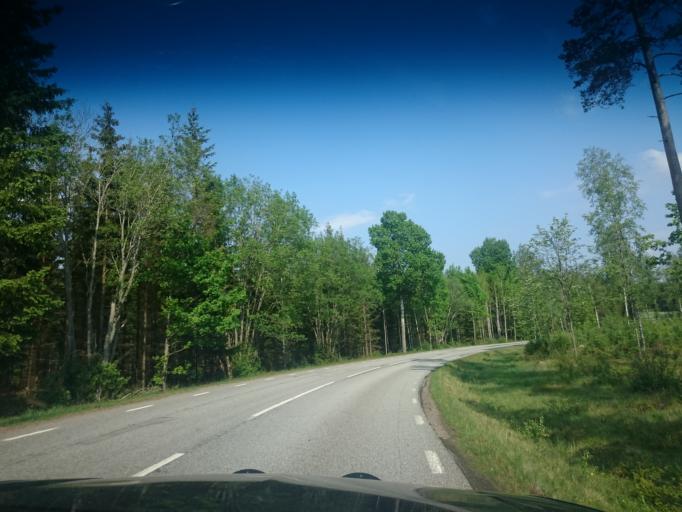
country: SE
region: Joenkoeping
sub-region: Vetlanda Kommun
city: Vetlanda
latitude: 57.3805
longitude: 15.0300
